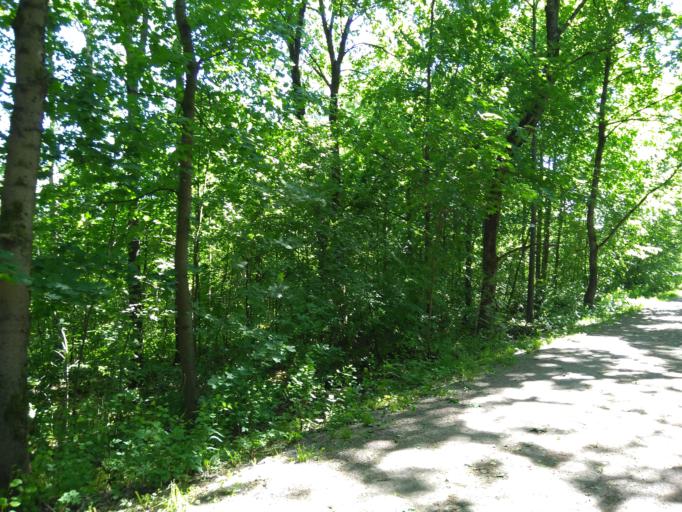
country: FI
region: Uusimaa
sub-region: Helsinki
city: Vantaa
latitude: 60.2293
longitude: 25.0050
